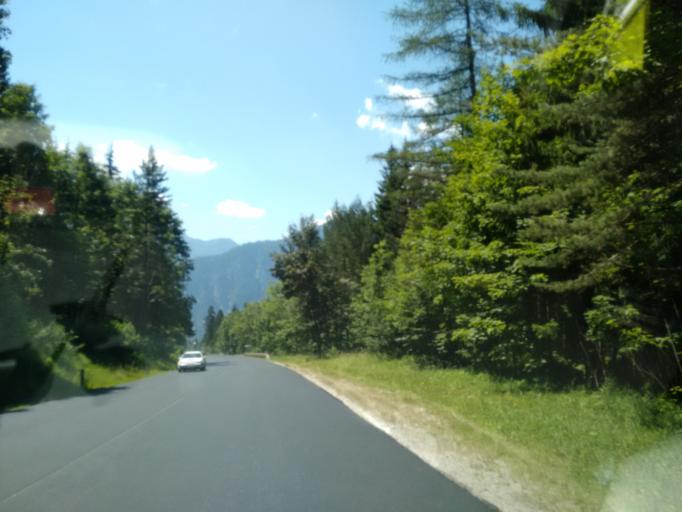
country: AT
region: Upper Austria
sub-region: Politischer Bezirk Gmunden
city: Bad Goisern
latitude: 47.6198
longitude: 13.6714
